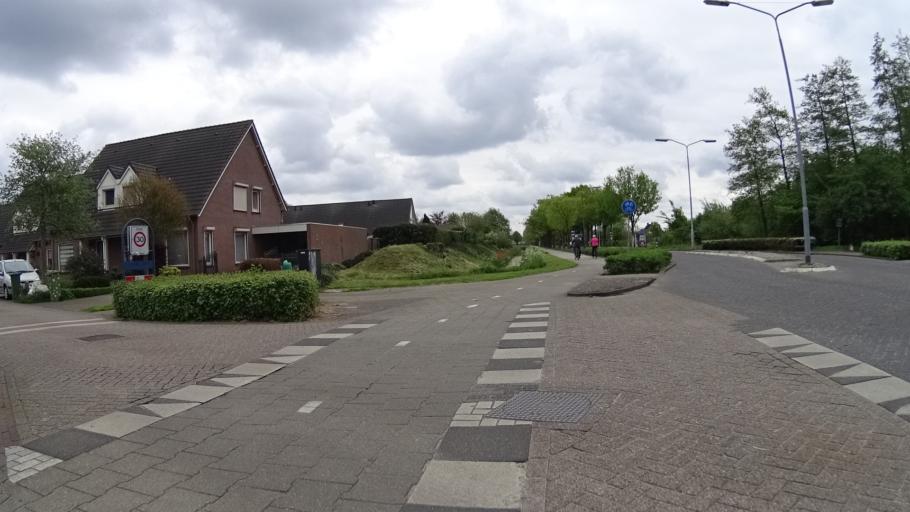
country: NL
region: North Brabant
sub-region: Gemeente Boekel
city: Boekel
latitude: 51.6004
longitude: 5.6859
